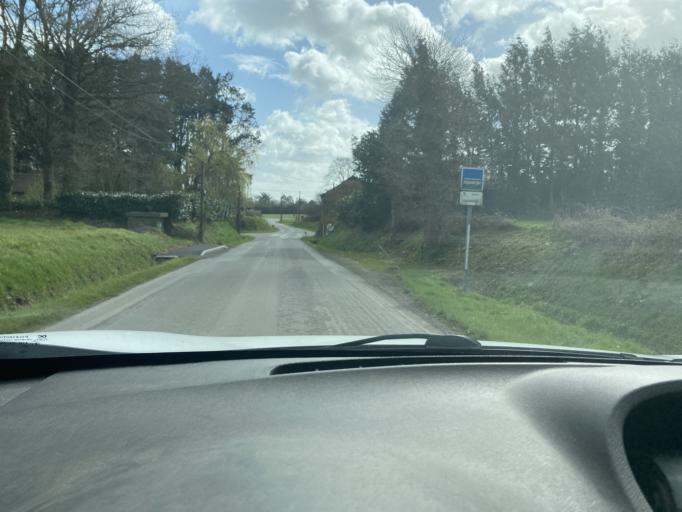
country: FR
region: Brittany
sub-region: Departement d'Ille-et-Vilaine
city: Melesse
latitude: 48.1855
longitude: -1.6963
